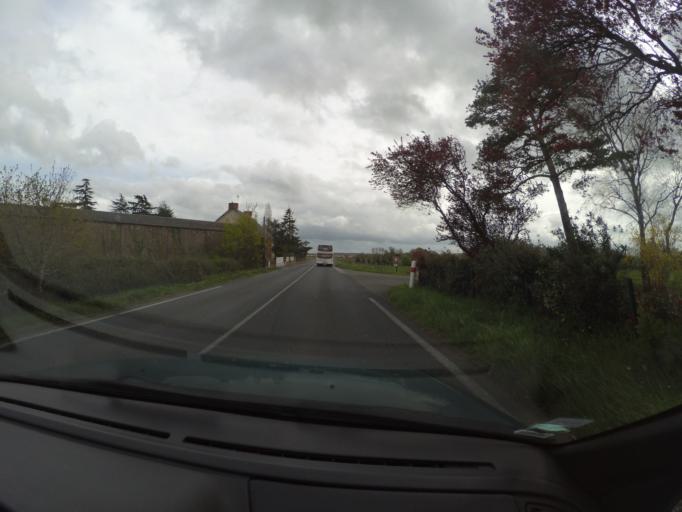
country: FR
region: Pays de la Loire
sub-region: Departement de Maine-et-Loire
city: Lire
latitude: 47.3145
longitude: -1.1628
